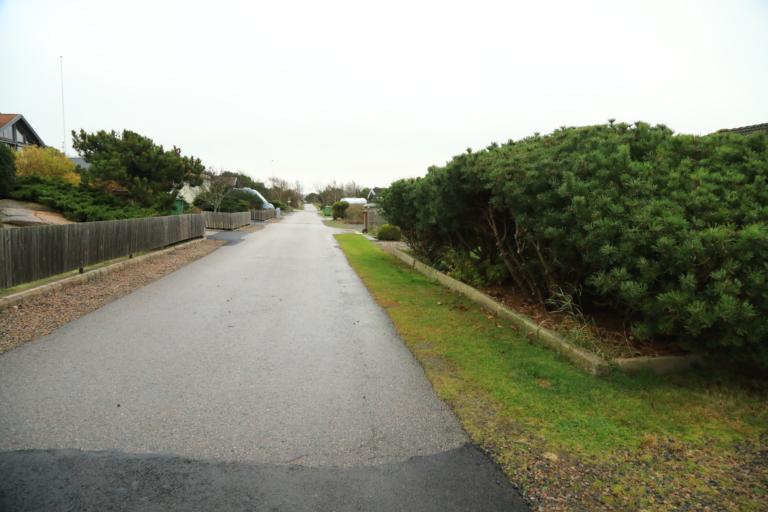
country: SE
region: Halland
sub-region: Varbergs Kommun
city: Varberg
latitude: 57.1696
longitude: 12.2110
